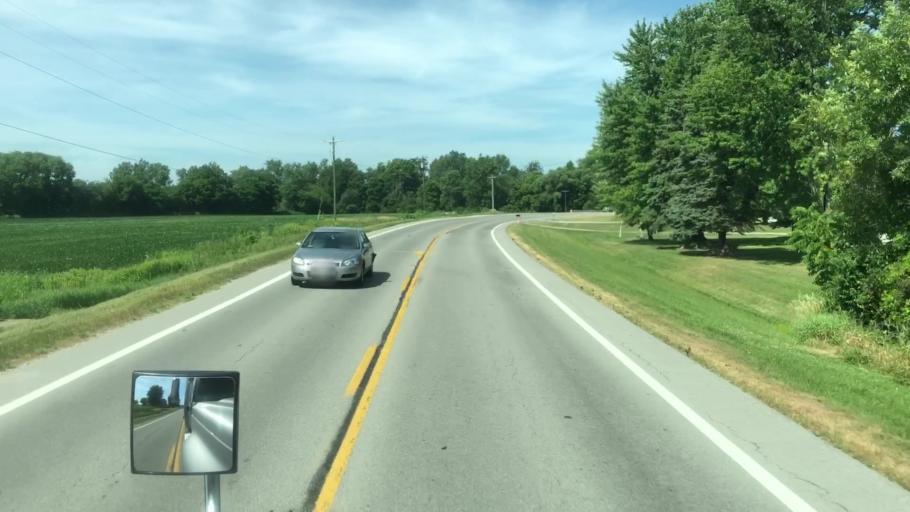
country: US
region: Ohio
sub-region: Sandusky County
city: Clyde
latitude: 41.3938
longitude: -83.0226
